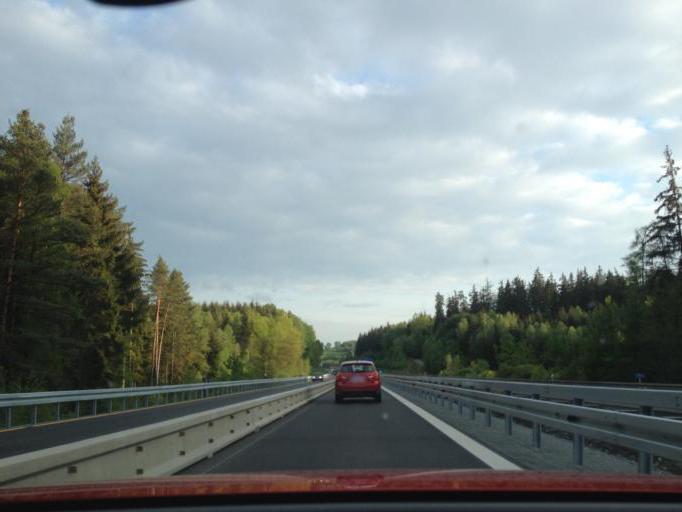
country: DE
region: Bavaria
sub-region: Upper Palatinate
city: Neustadt an der Waldnaab
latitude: 49.7487
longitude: 12.1538
